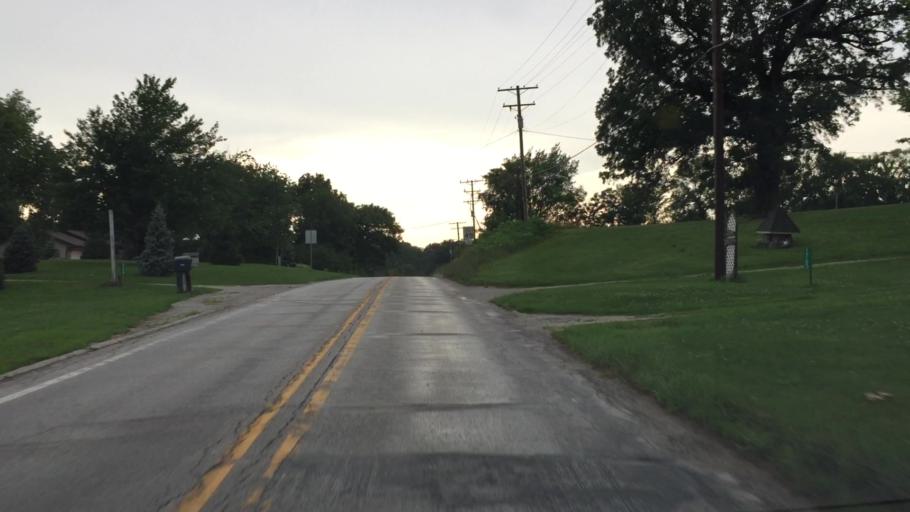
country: US
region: Illinois
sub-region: Hancock County
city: Warsaw
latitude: 40.3565
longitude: -91.4203
